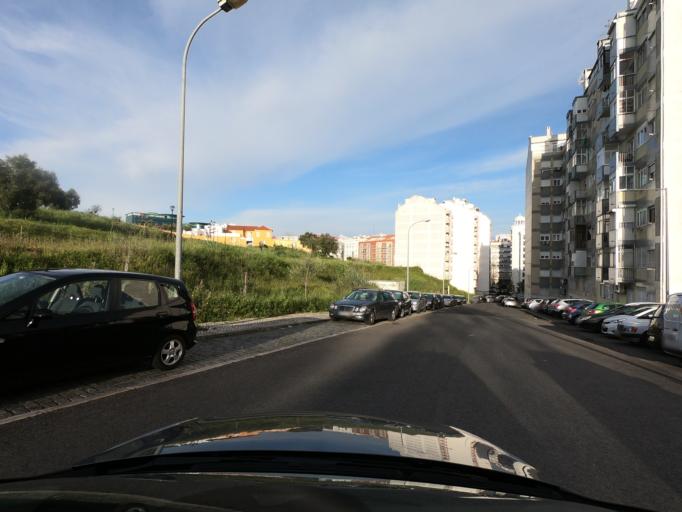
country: PT
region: Lisbon
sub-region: Odivelas
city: Pontinha
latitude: 38.7509
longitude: -9.1936
